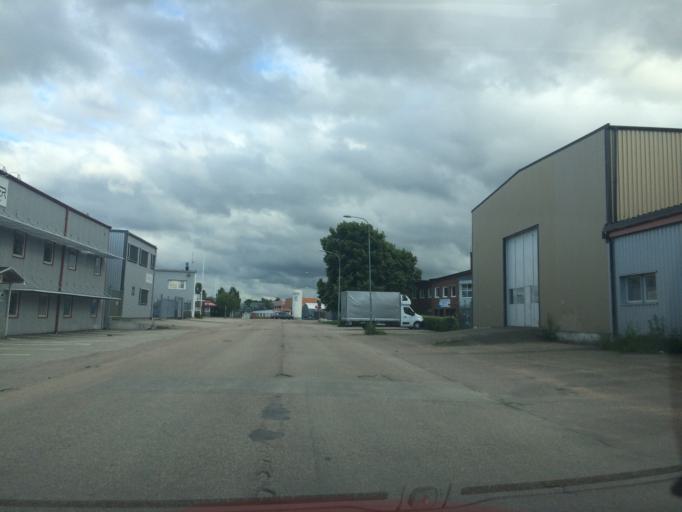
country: SE
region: Vaestra Goetaland
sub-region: Vanersborgs Kommun
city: Vanersborg
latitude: 58.3795
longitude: 12.3409
